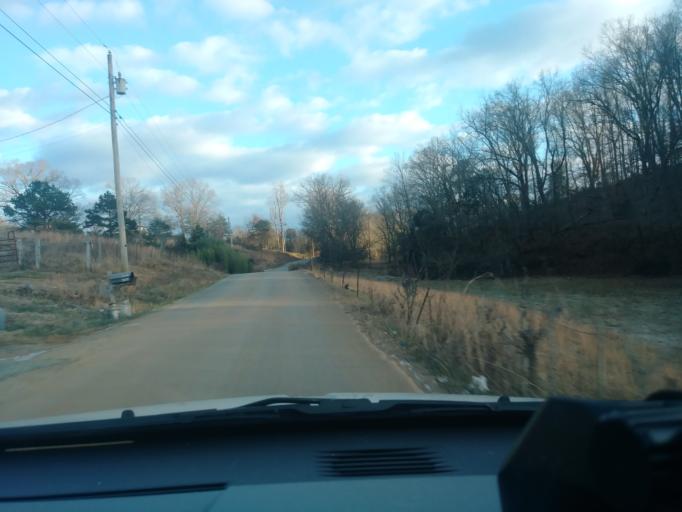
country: US
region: Tennessee
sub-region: Greene County
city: Greeneville
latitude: 36.0785
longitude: -82.8886
